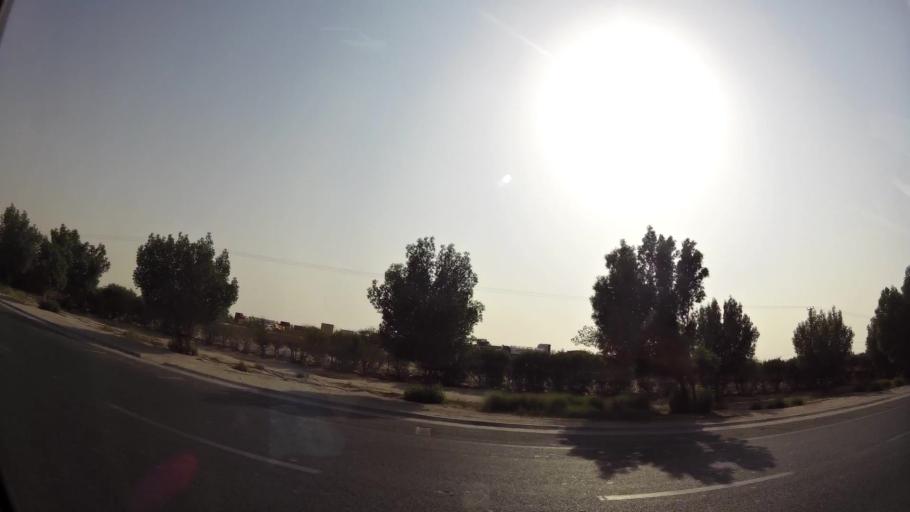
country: KW
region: Muhafazat al Jahra'
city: Al Jahra'
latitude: 29.3149
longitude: 47.7697
